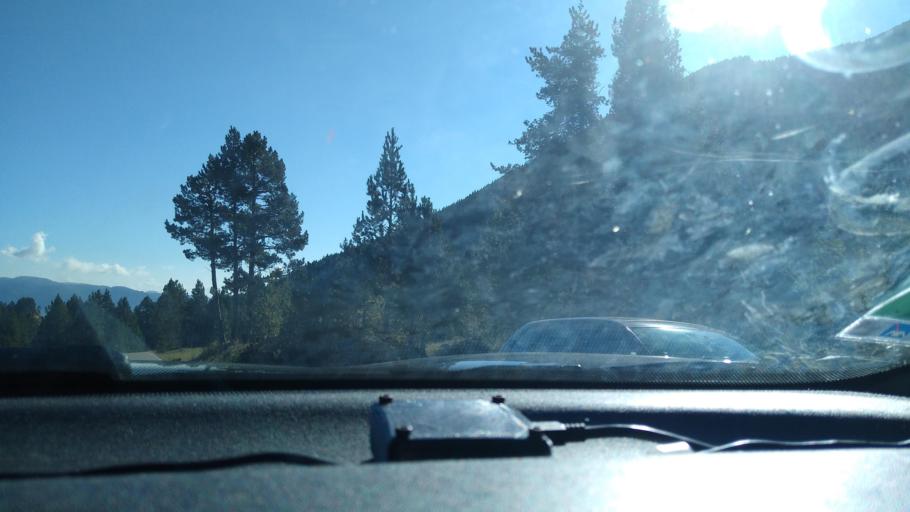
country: ES
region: Catalonia
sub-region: Provincia de Barcelona
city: Vallcebre
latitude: 42.2007
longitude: 1.7757
